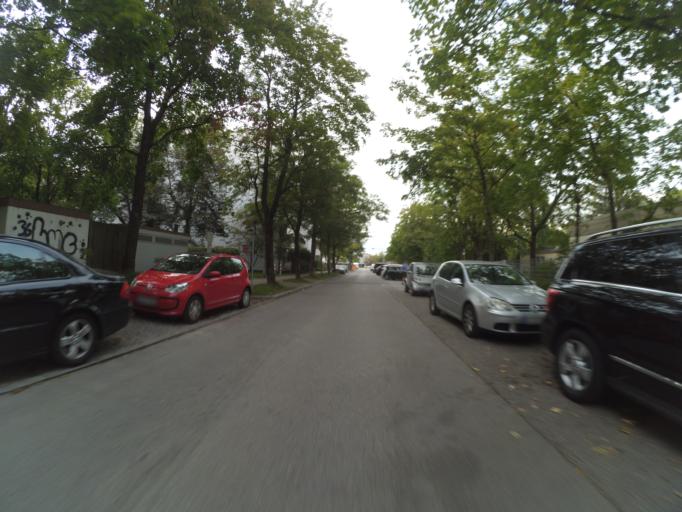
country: DE
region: Bavaria
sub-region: Upper Bavaria
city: Munich
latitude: 48.1852
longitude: 11.5357
